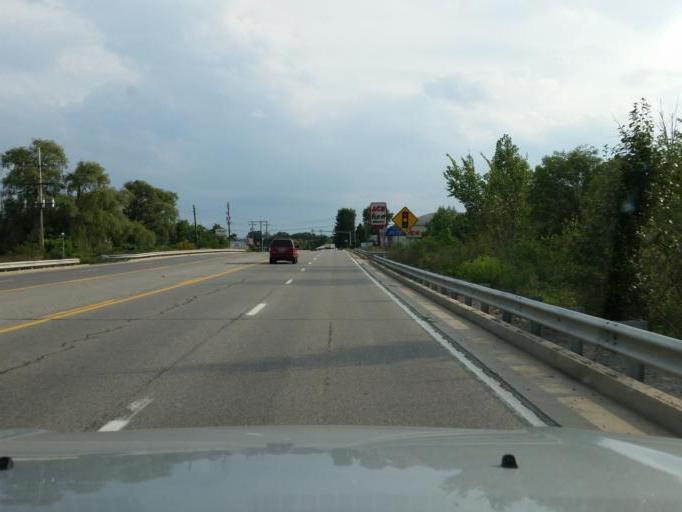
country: US
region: Pennsylvania
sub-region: Blair County
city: Duncansville
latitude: 40.4287
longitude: -78.4400
